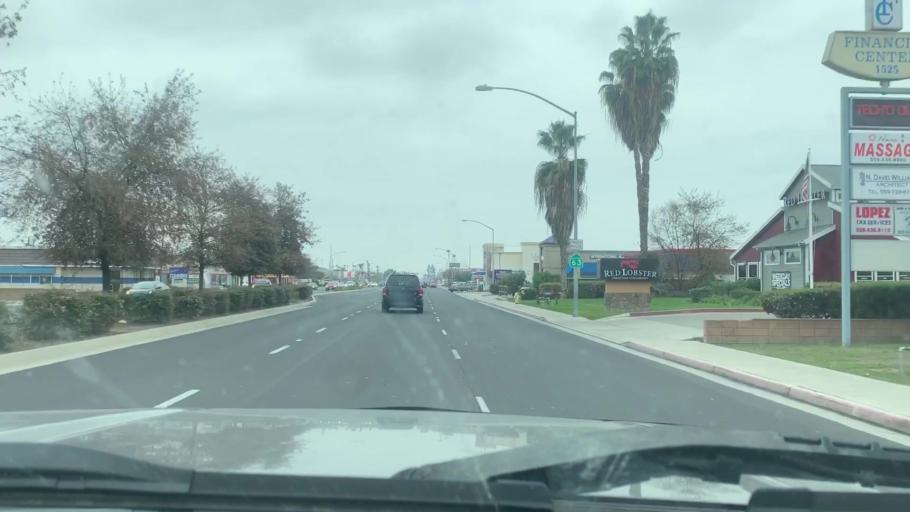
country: US
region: California
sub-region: Tulare County
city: Visalia
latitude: 36.3170
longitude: -119.3140
